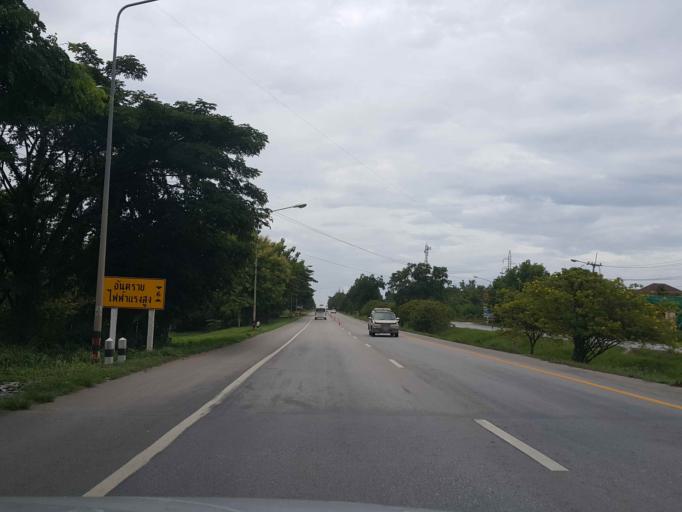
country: TH
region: Lampang
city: Thoen
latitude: 17.6114
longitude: 99.2290
